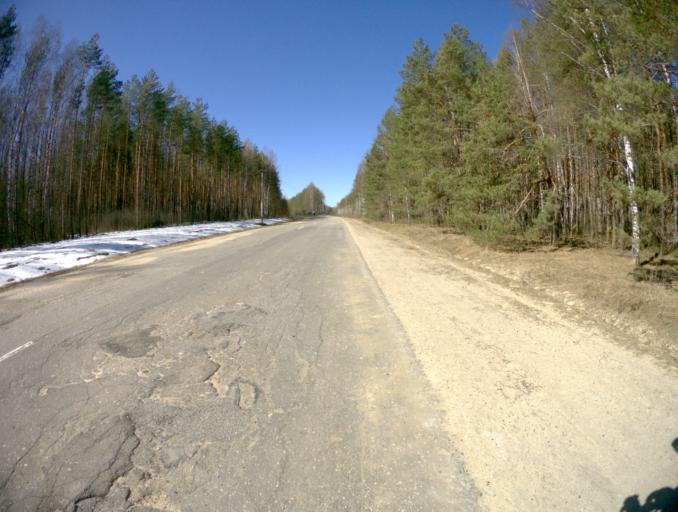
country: RU
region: Vladimir
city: Orgtrud
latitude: 56.3470
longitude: 40.7628
